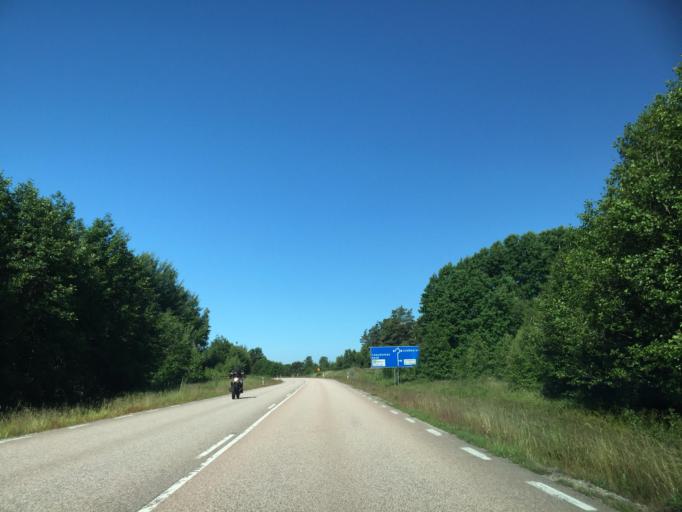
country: SE
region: Vaestra Goetaland
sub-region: Tanums Kommun
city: Tanumshede
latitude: 58.8121
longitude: 11.2703
